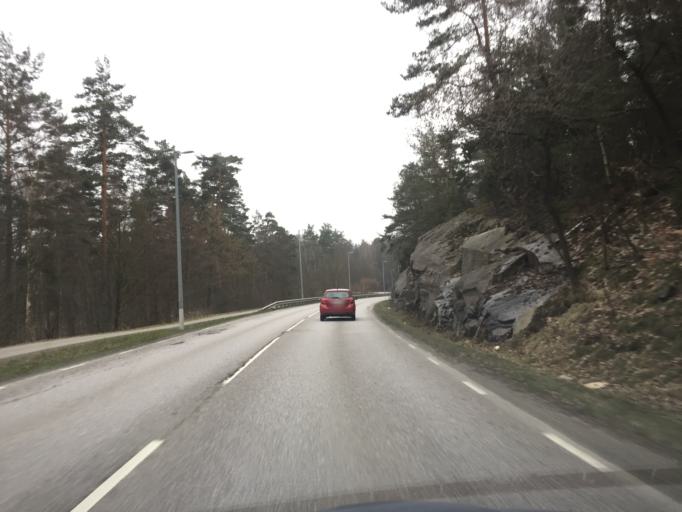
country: SE
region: Vaestra Goetaland
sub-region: Goteborg
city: Eriksbo
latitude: 57.7666
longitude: 12.0743
